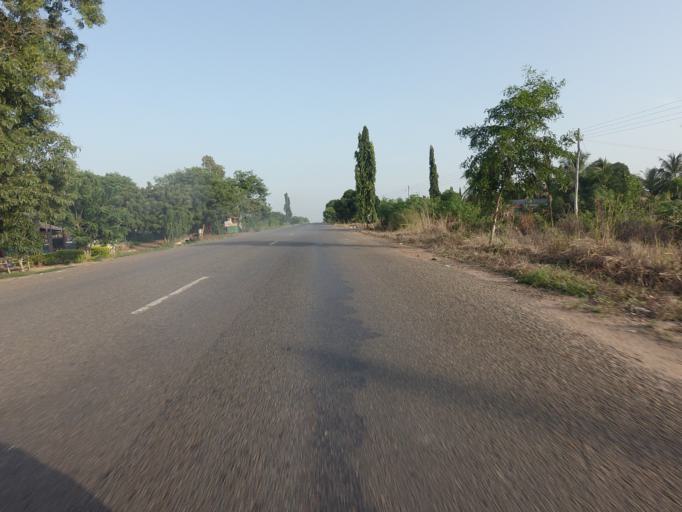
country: GH
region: Volta
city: Anloga
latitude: 6.0155
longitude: 0.6663
